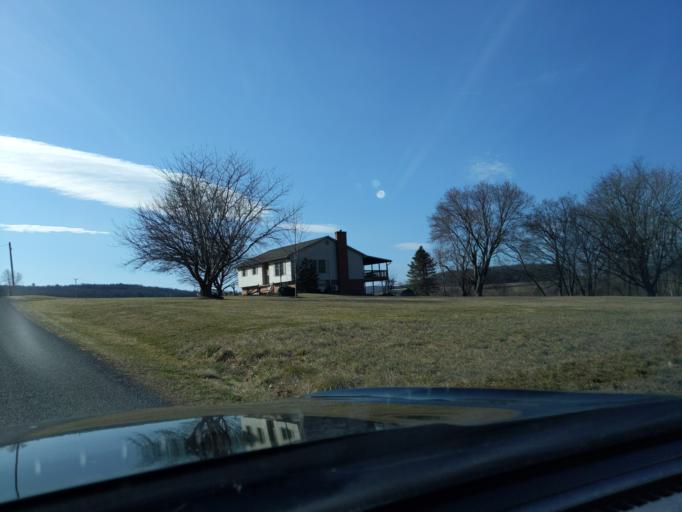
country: US
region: Pennsylvania
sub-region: Blair County
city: Martinsburg
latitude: 40.3933
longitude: -78.2742
